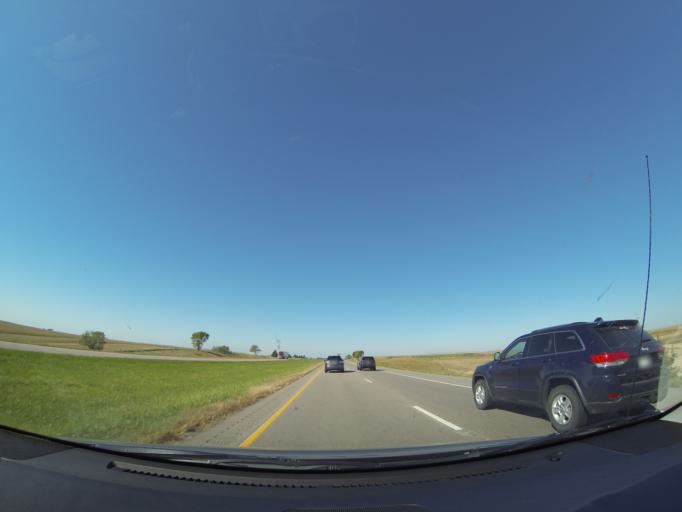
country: US
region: Nebraska
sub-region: Saline County
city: Friend
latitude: 40.8218
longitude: -97.3235
